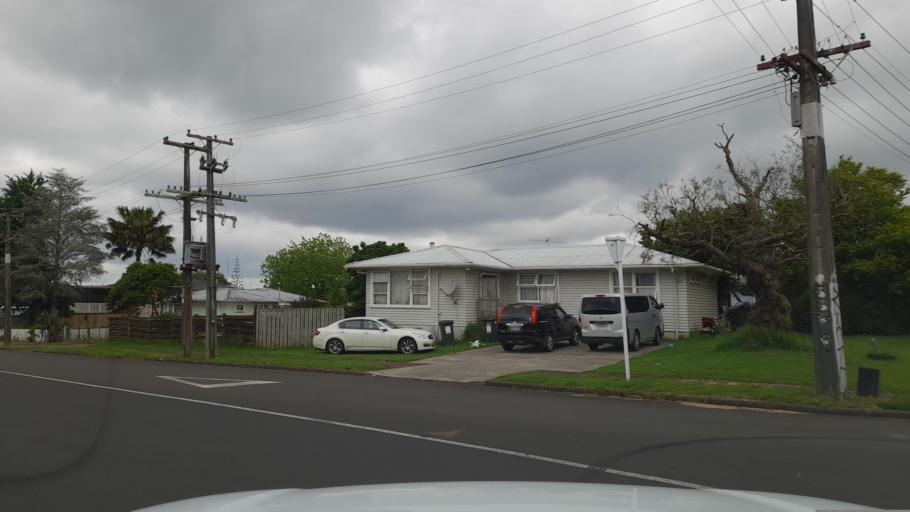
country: NZ
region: Northland
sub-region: Far North District
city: Waimate North
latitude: -35.4042
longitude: 173.7881
